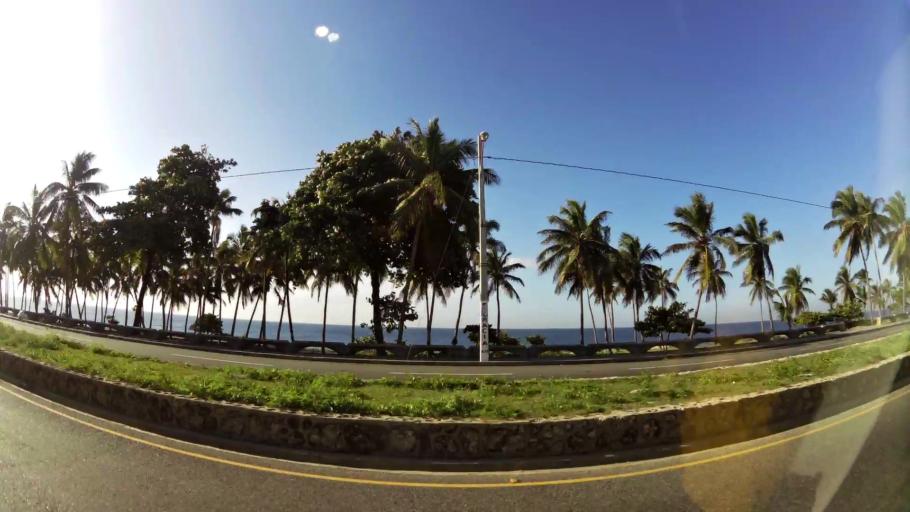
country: DO
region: Santo Domingo
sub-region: Santo Domingo
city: Santo Domingo Este
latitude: 18.4679
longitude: -69.8410
